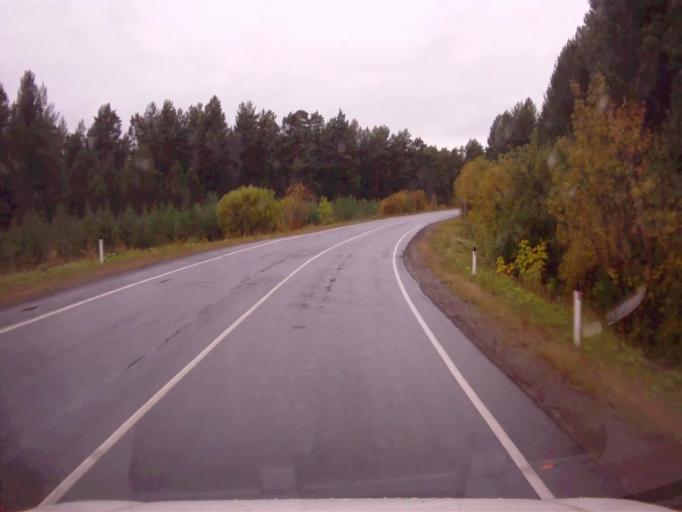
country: RU
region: Chelyabinsk
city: Verkhniy Ufaley
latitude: 56.0518
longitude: 60.1672
